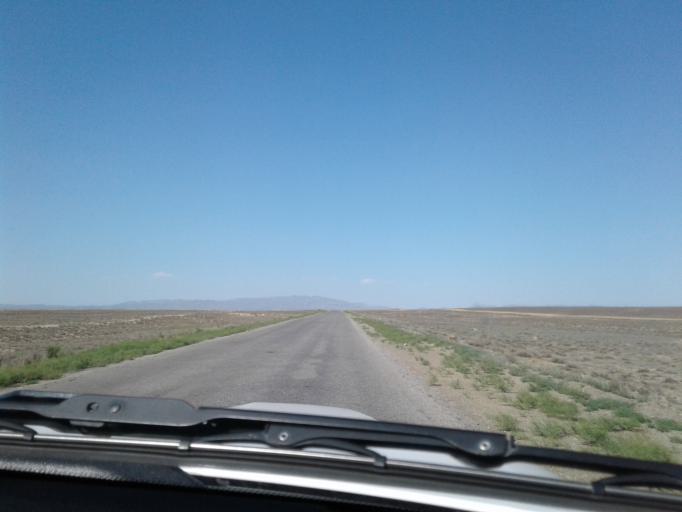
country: TM
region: Balkan
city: Magtymguly
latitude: 38.6139
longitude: 56.2194
